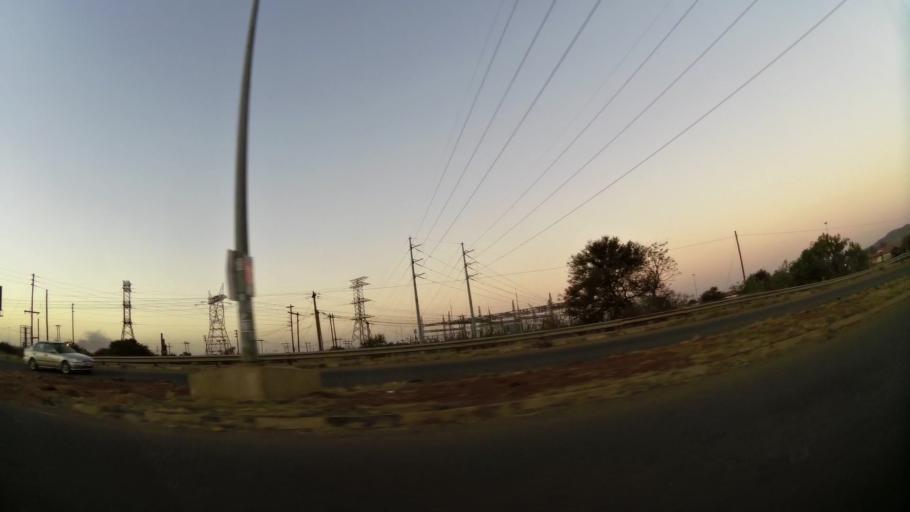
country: ZA
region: North-West
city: Ga-Rankuwa
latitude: -25.5874
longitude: 27.9887
